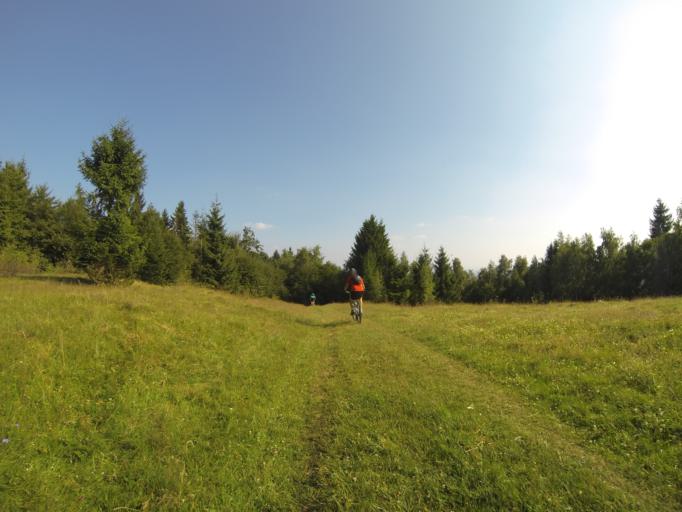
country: RO
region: Valcea
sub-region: Comuna Vaideeni
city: Vaideeni
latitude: 45.2253
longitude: 23.9675
